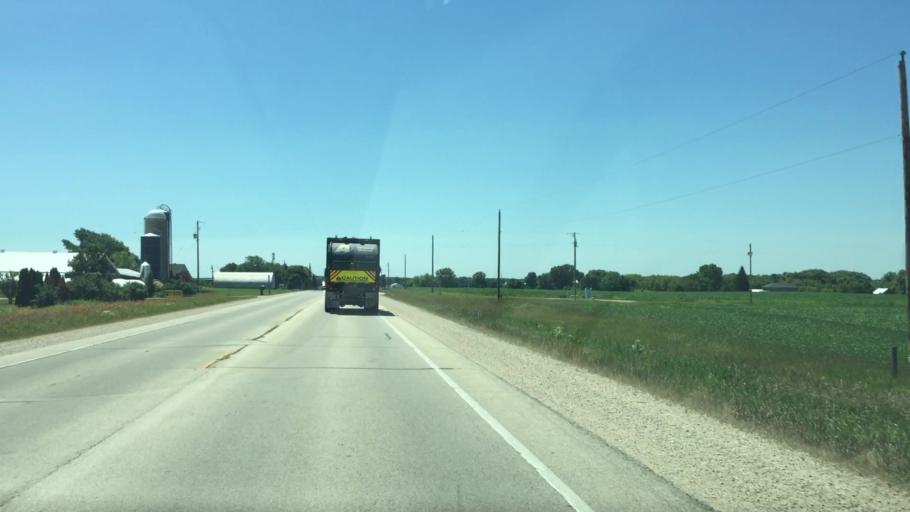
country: US
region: Wisconsin
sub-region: Calumet County
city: Hilbert
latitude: 44.0887
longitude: -88.1637
